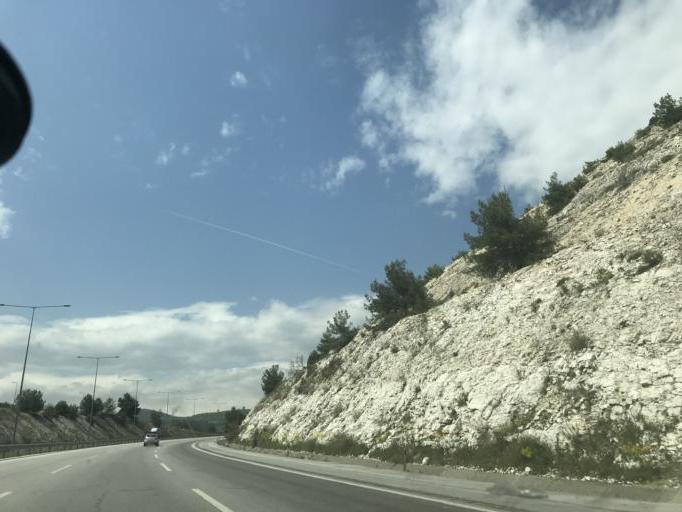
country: TR
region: Mersin
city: Tarsus
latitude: 37.1389
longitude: 34.8438
